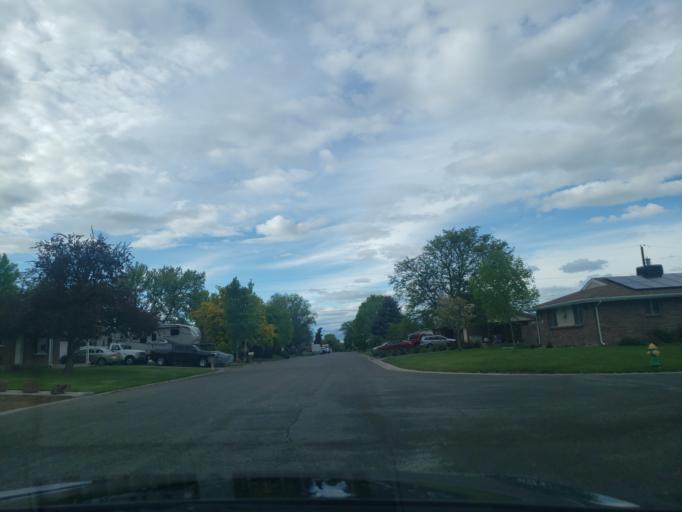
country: US
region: Colorado
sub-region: Mesa County
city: Redlands
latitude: 39.0943
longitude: -108.6588
